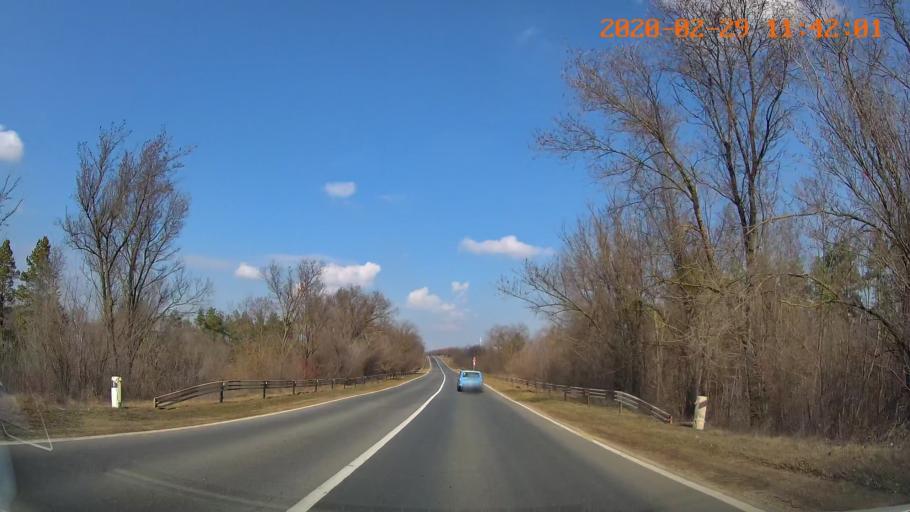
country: MD
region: Rezina
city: Saharna
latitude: 47.6787
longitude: 29.0146
